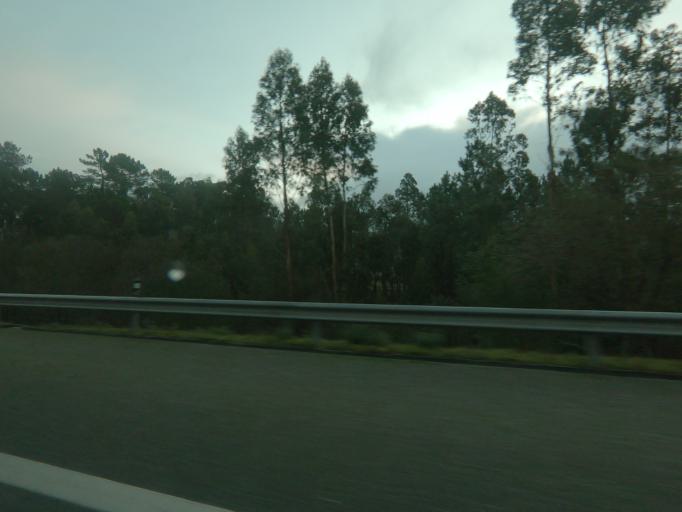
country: PT
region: Braga
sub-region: Barcelos
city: Galegos
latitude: 41.6510
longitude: -8.5506
